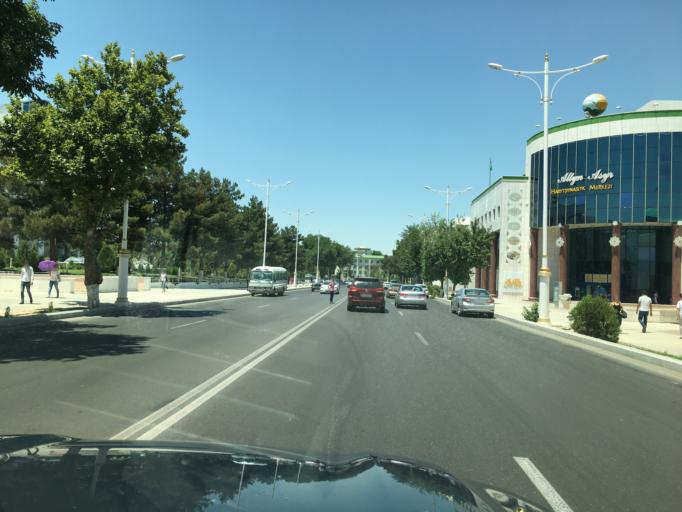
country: TM
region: Ahal
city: Ashgabat
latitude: 37.9403
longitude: 58.3791
